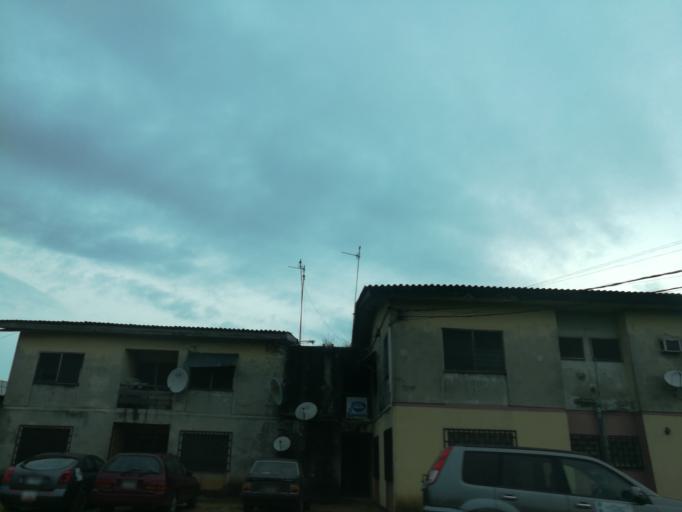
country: NG
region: Rivers
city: Port Harcourt
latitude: 4.8180
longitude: 7.0282
